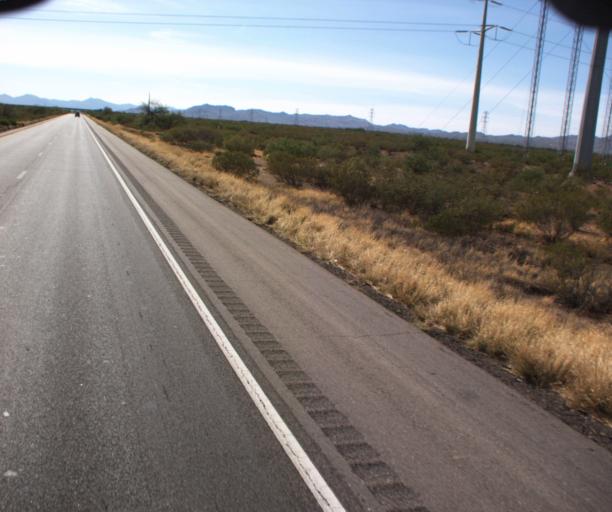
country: US
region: Arizona
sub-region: Pima County
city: Vail
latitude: 32.0326
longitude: -110.7290
